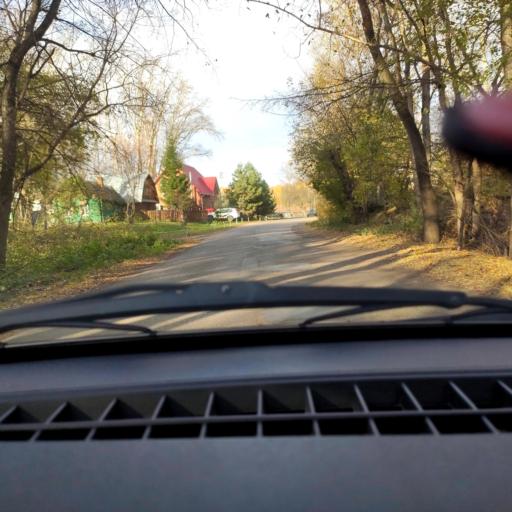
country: RU
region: Bashkortostan
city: Ufa
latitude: 54.7852
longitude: 56.1631
